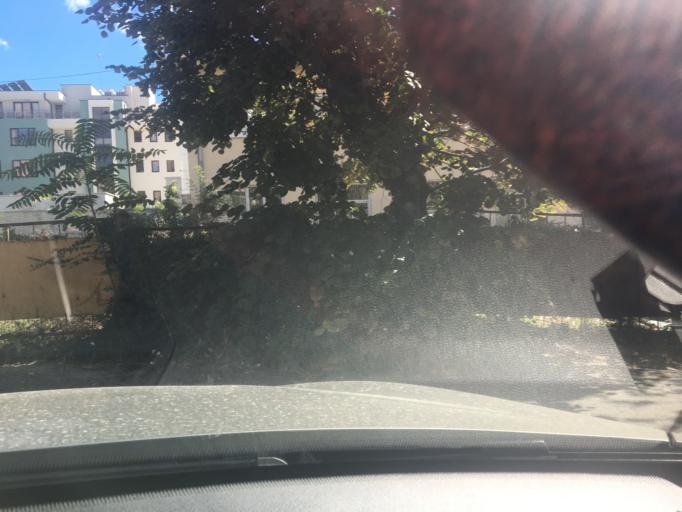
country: BG
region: Burgas
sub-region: Obshtina Burgas
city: Burgas
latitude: 42.5017
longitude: 27.4751
